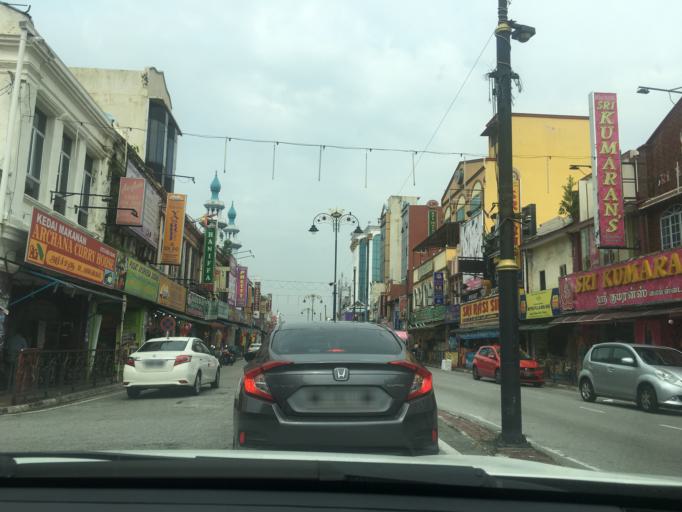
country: MY
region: Selangor
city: Klang
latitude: 3.0405
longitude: 101.4469
